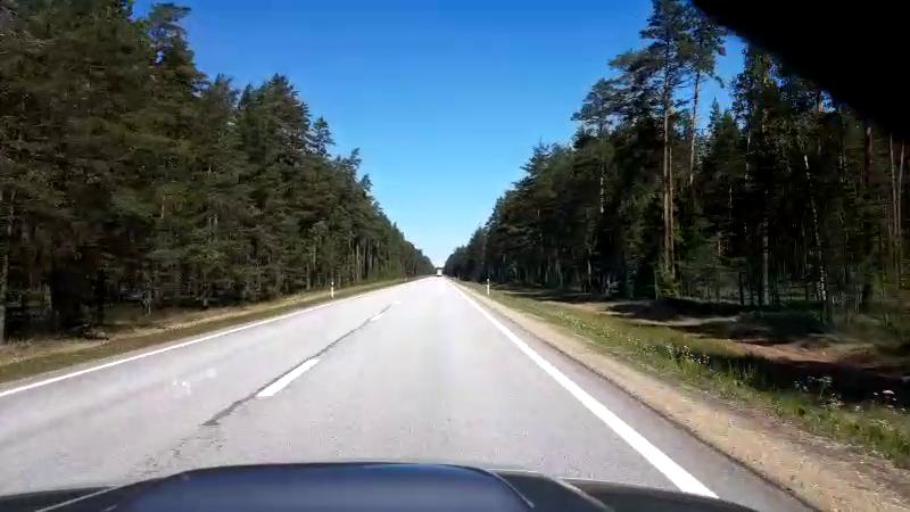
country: LV
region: Salacgrivas
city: Salacgriva
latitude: 57.5547
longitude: 24.4333
